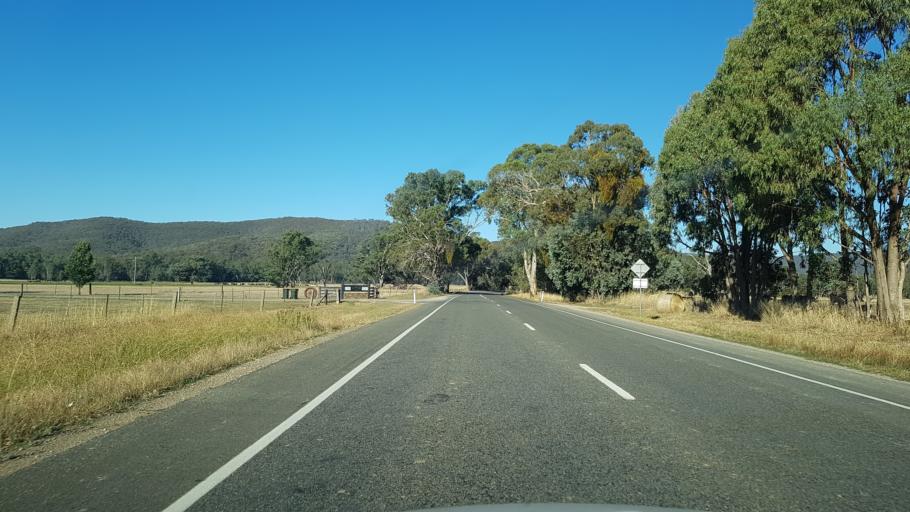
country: AU
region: Victoria
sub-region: Wangaratta
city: Wangaratta
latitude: -36.6098
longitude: 146.3915
